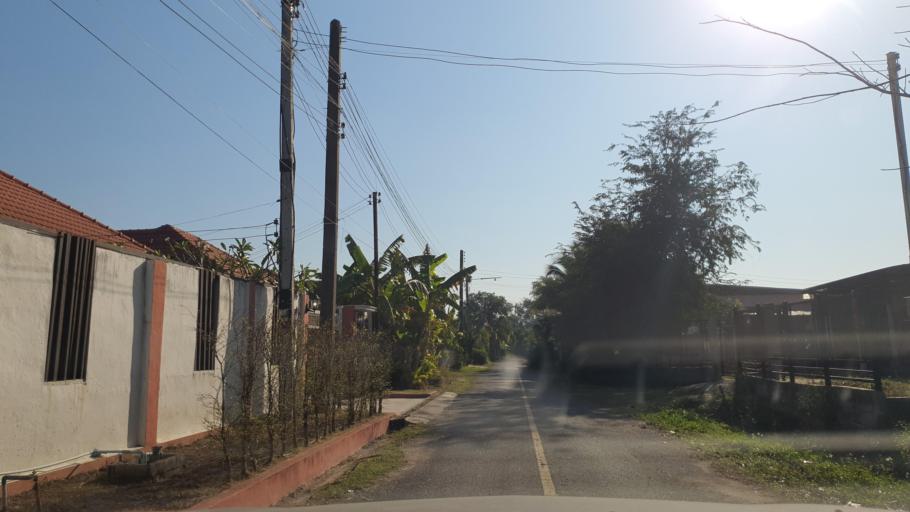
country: TH
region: Chiang Mai
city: Saraphi
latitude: 18.6911
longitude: 99.0752
